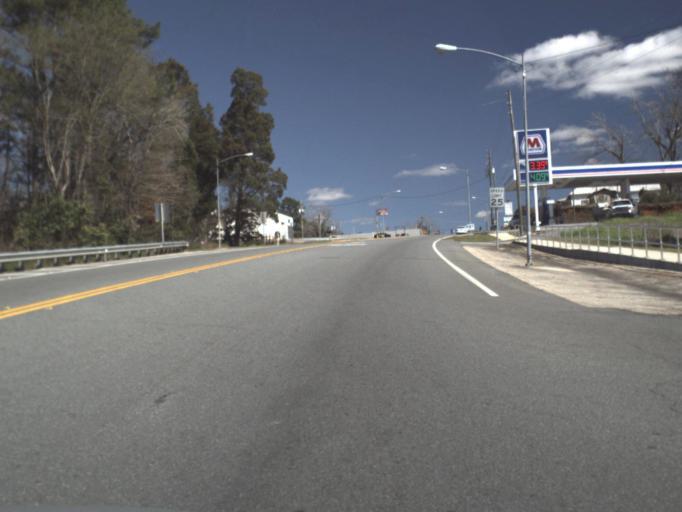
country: US
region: Florida
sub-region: Gadsden County
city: Chattahoochee
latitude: 30.7048
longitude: -84.8511
